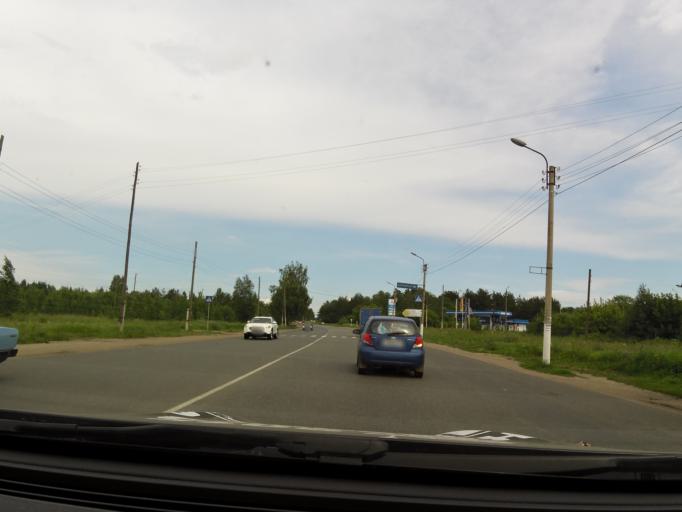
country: RU
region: Kirov
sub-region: Kirovo-Chepetskiy Rayon
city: Kirov
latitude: 58.6165
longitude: 49.7651
